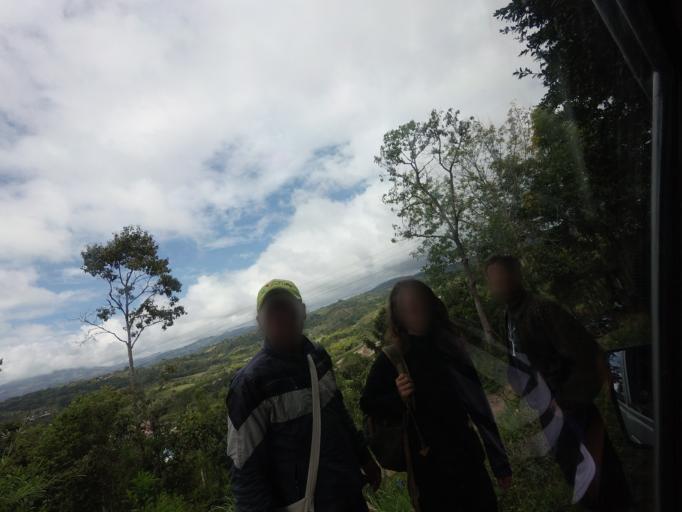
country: CO
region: Huila
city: San Agustin
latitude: 1.8880
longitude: -76.2717
